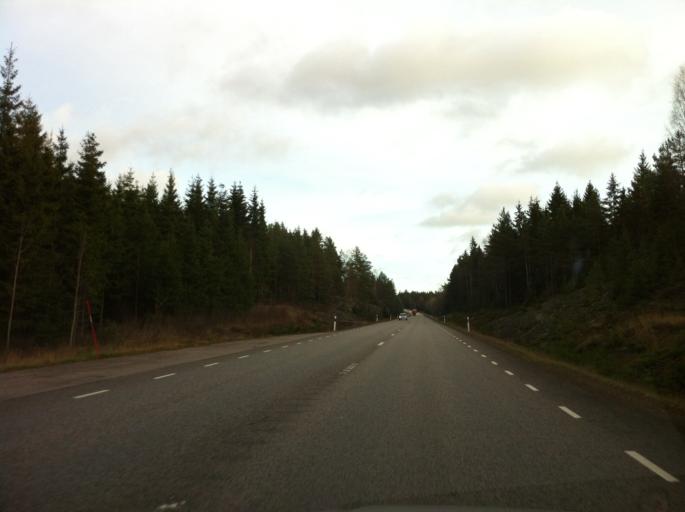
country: SE
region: Kronoberg
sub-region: Uppvidinge Kommun
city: Aseda
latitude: 57.1448
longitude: 15.2934
